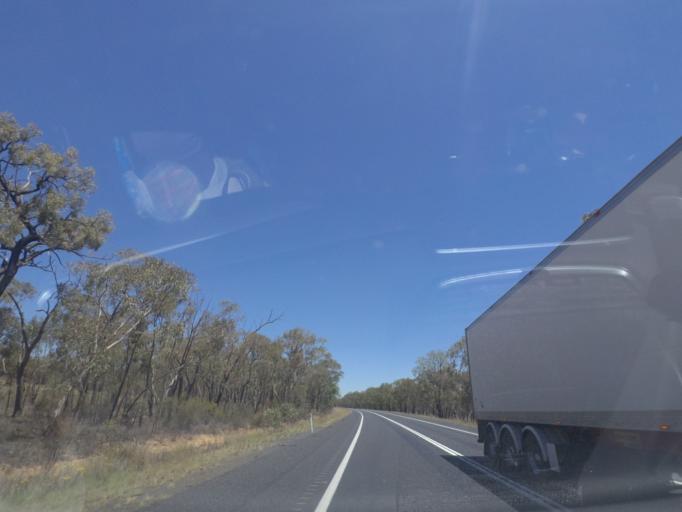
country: AU
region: New South Wales
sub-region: Warrumbungle Shire
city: Coonabarabran
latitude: -31.2085
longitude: 149.3316
